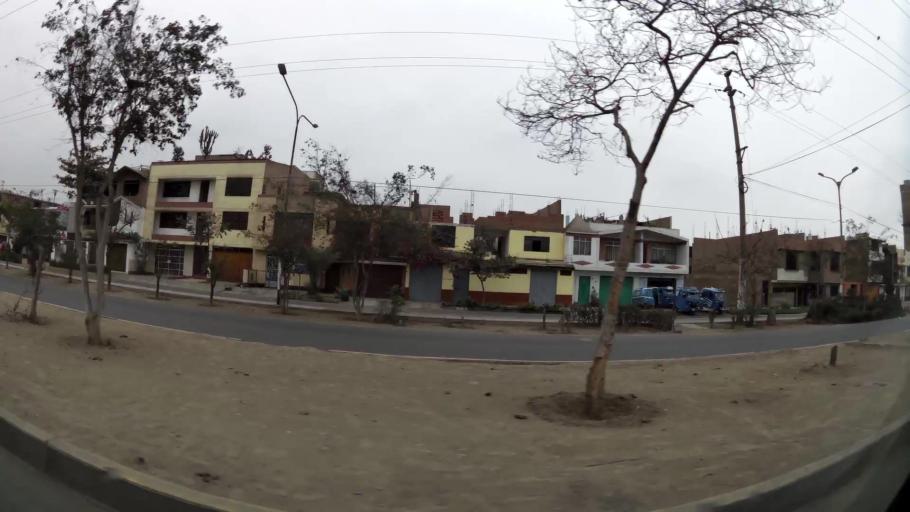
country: PE
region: Lima
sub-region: Lima
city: Independencia
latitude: -11.9453
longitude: -77.0639
